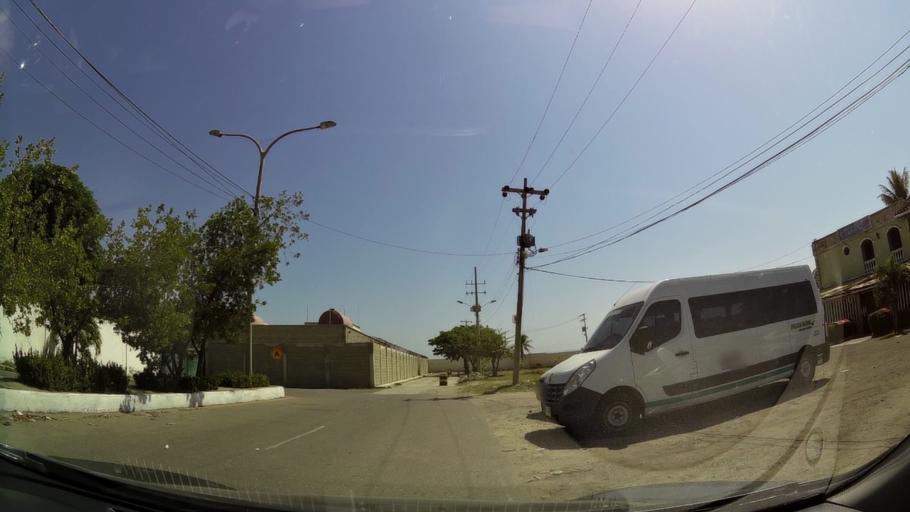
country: CO
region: Bolivar
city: Cartagena
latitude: 10.4441
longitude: -75.5147
